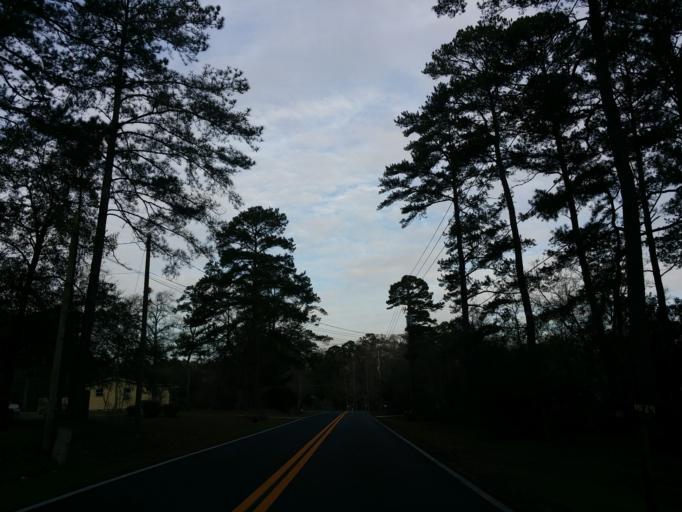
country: US
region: Florida
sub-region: Leon County
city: Tallahassee
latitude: 30.4727
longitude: -84.2165
